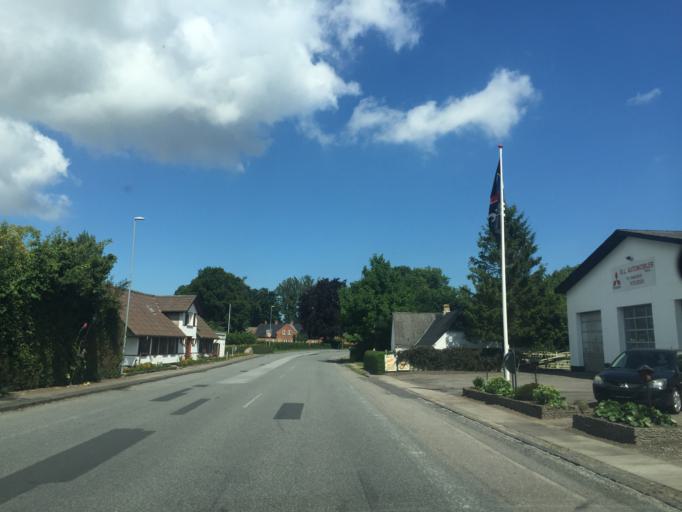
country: DK
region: South Denmark
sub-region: Nordfyns Kommune
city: Otterup
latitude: 55.5452
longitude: 10.3917
